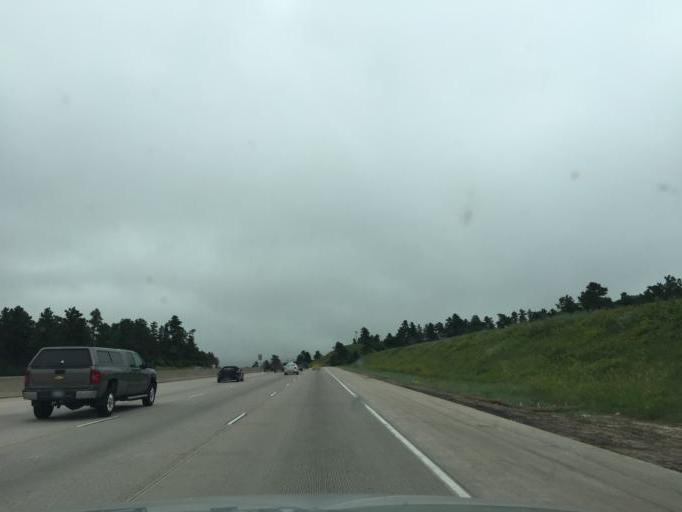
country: US
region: Colorado
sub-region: Douglas County
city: Castle Pines
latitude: 39.4382
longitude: -104.8774
